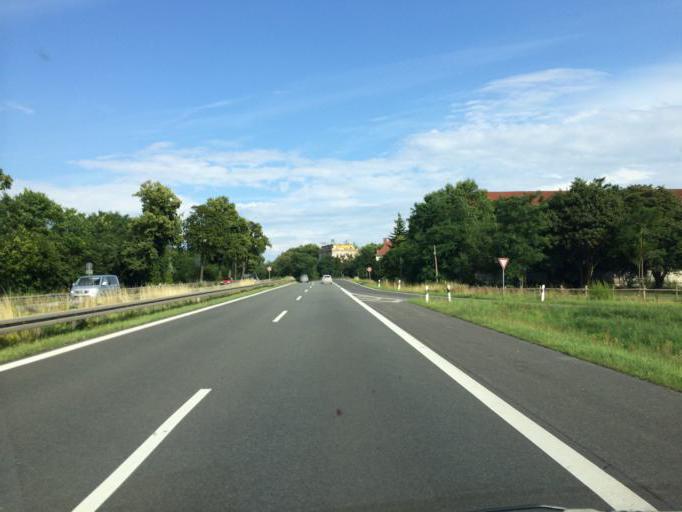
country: DE
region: Brandenburg
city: Brieselang
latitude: 52.5337
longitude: 13.0009
